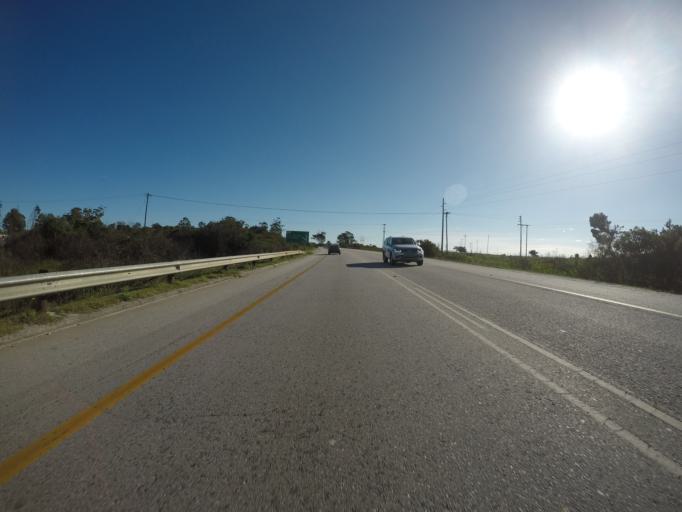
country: ZA
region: Eastern Cape
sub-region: Cacadu District Municipality
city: Jeffrey's Bay
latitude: -33.8920
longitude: 25.1375
